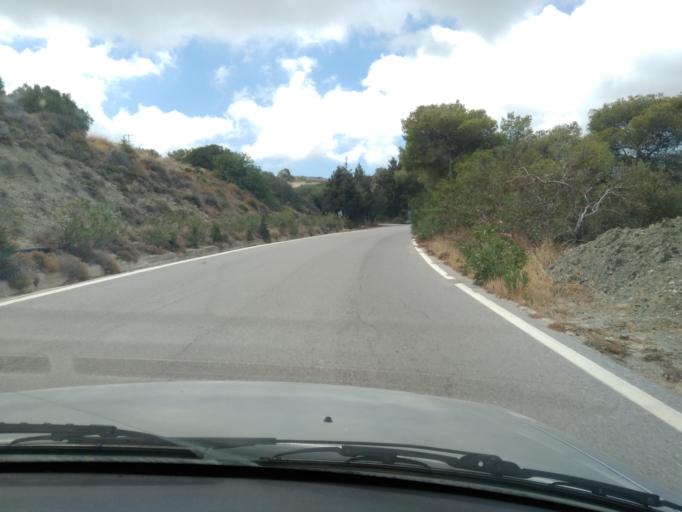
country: GR
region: Crete
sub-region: Nomos Lasithiou
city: Makry-Gialos
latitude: 35.0662
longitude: 26.0471
